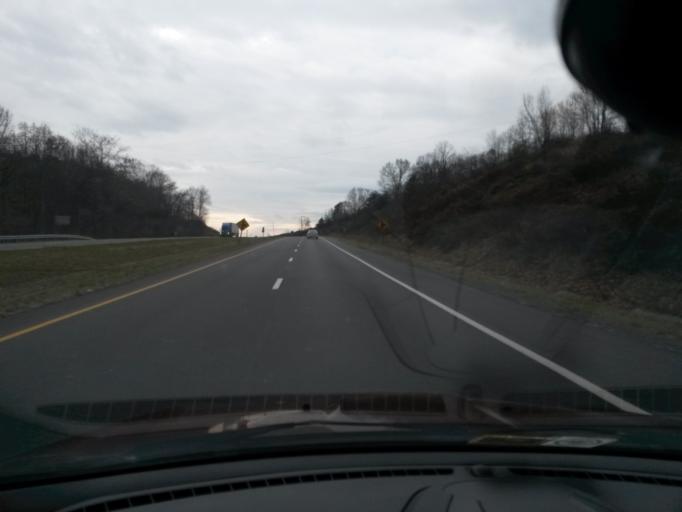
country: US
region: Virginia
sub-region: Botetourt County
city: Cloverdale
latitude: 37.3654
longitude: -79.8867
